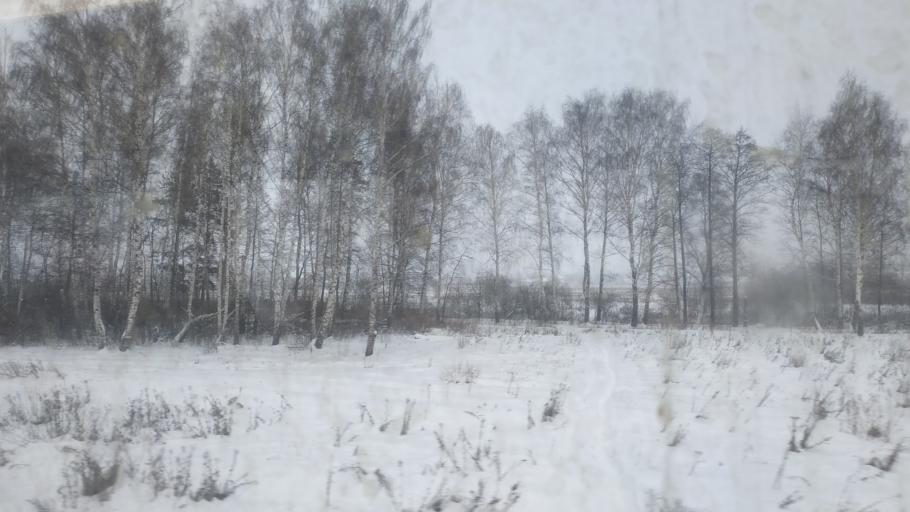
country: RU
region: Moskovskaya
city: Malyshevo
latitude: 55.5242
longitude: 38.3234
